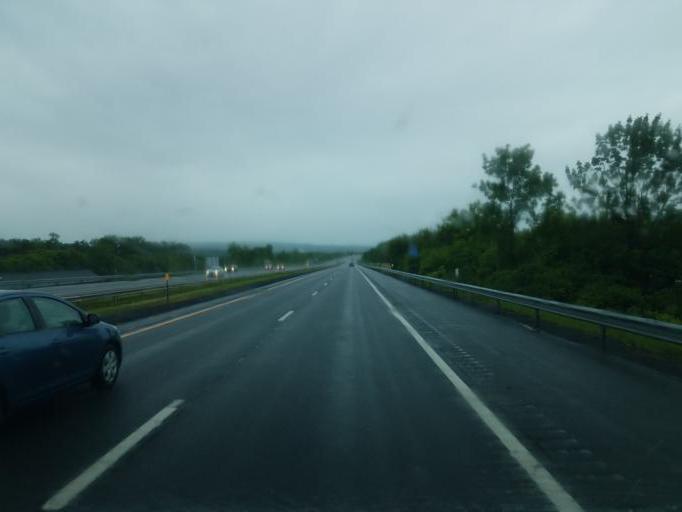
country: US
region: New York
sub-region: Herkimer County
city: Mohawk
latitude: 43.0177
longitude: -74.9962
